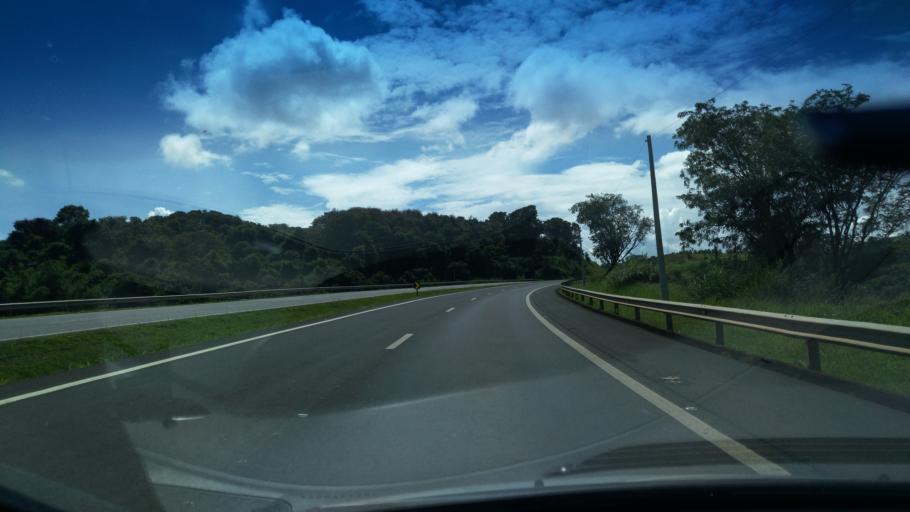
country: BR
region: Sao Paulo
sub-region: Santo Antonio Do Jardim
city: Espirito Santo do Pinhal
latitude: -22.2105
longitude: -46.7836
